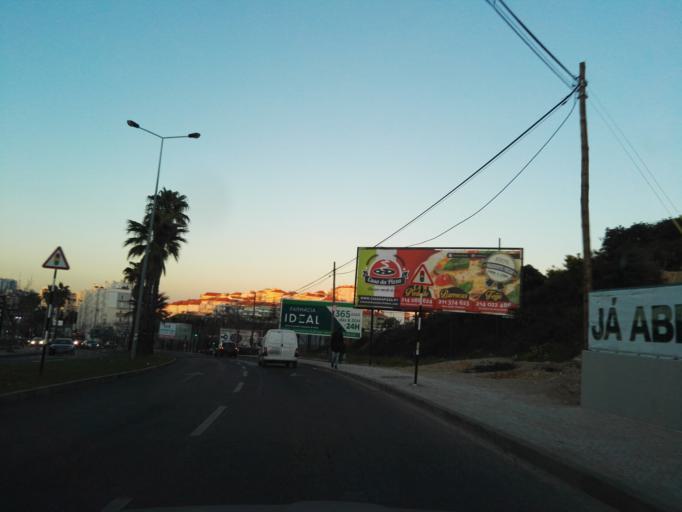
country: PT
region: Setubal
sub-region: Almada
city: Piedade
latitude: 38.6632
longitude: -9.1627
